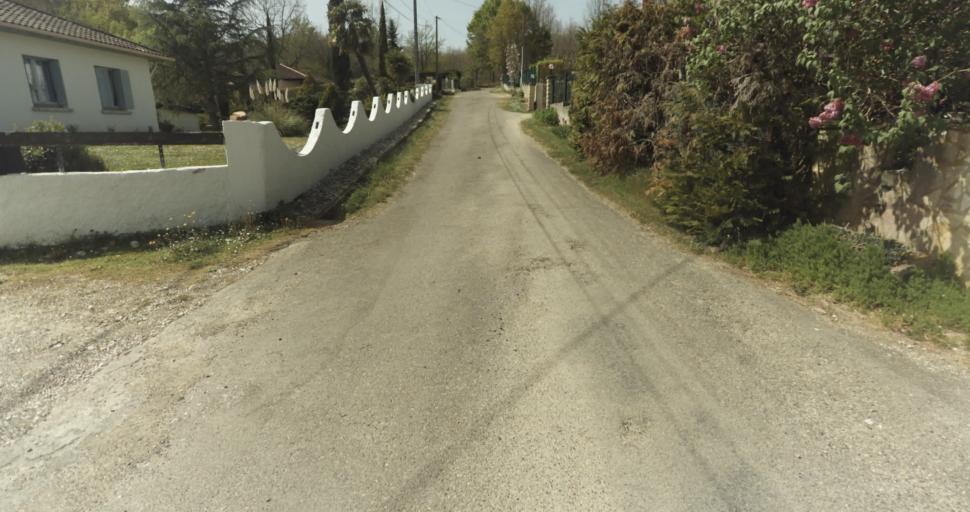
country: FR
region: Midi-Pyrenees
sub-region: Departement du Tarn-et-Garonne
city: Moissac
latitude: 44.1387
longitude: 1.0976
